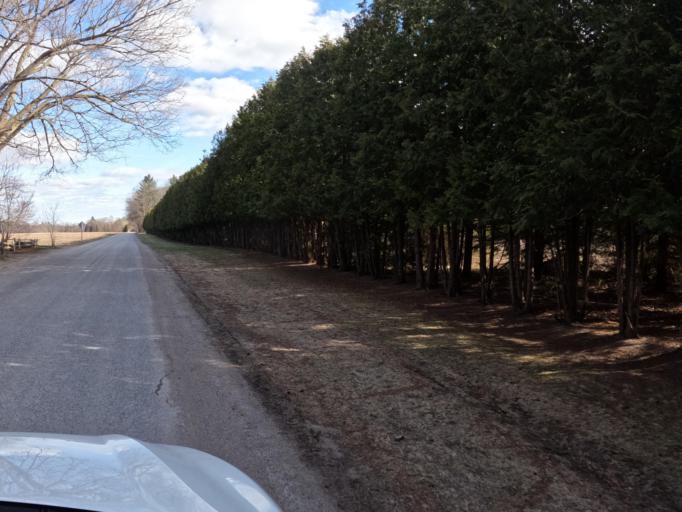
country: CA
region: Ontario
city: Norfolk County
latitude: 42.7777
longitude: -80.5195
